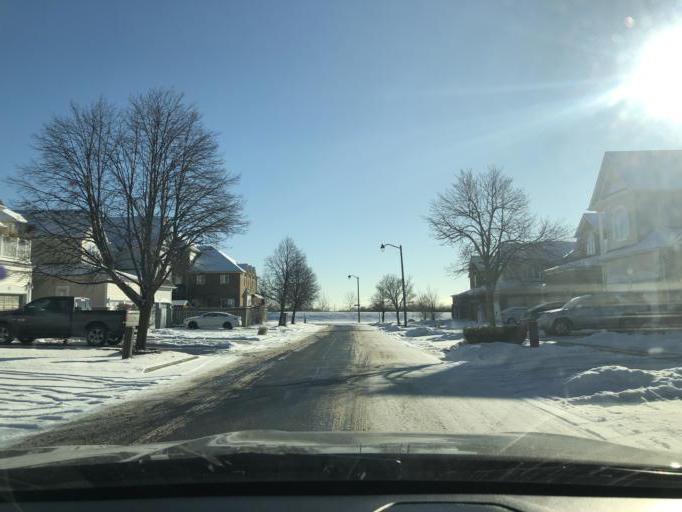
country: CA
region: Ontario
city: Scarborough
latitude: 43.7722
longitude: -79.1401
